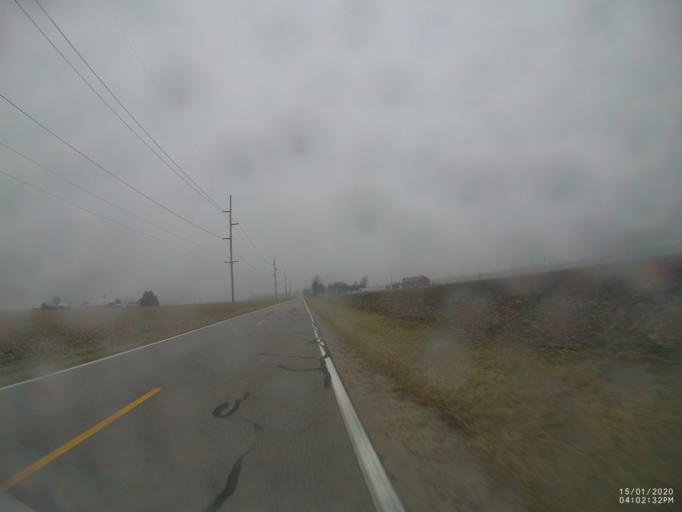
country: US
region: Ohio
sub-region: Sandusky County
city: Woodville
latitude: 41.4138
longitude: -83.3737
